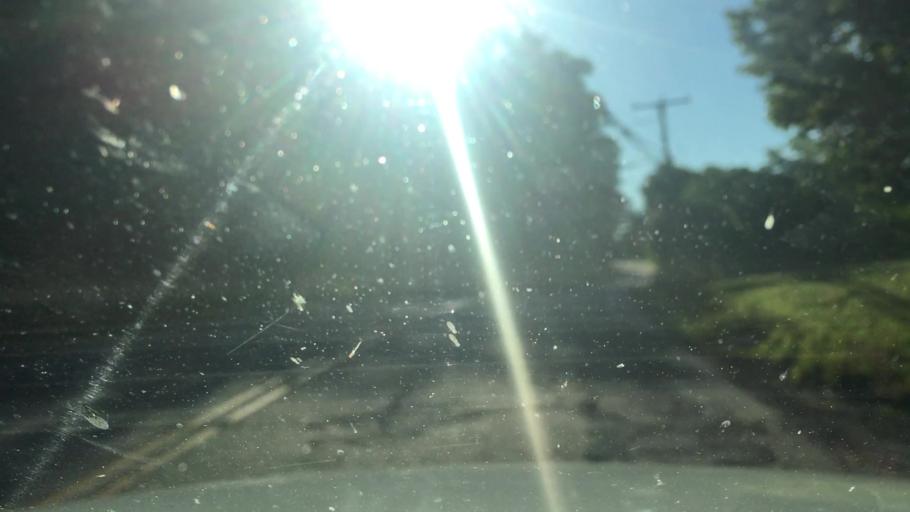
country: US
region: New Hampshire
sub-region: Rockingham County
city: Sandown
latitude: 42.9216
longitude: -71.1765
